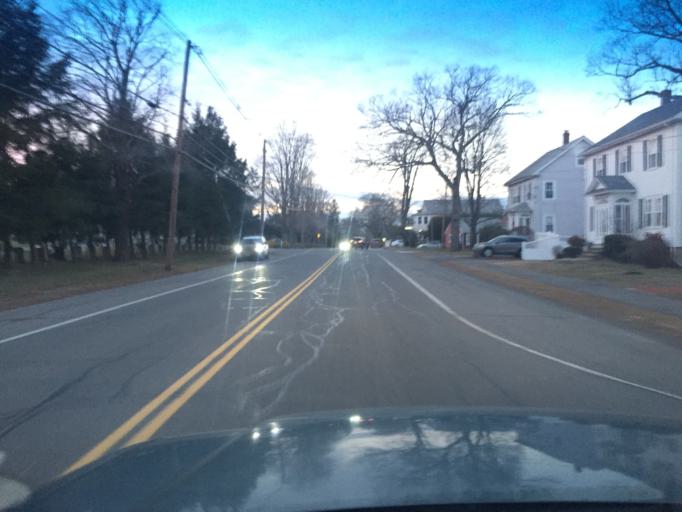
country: US
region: Massachusetts
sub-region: Norfolk County
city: Norwood
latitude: 42.1954
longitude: -71.2140
